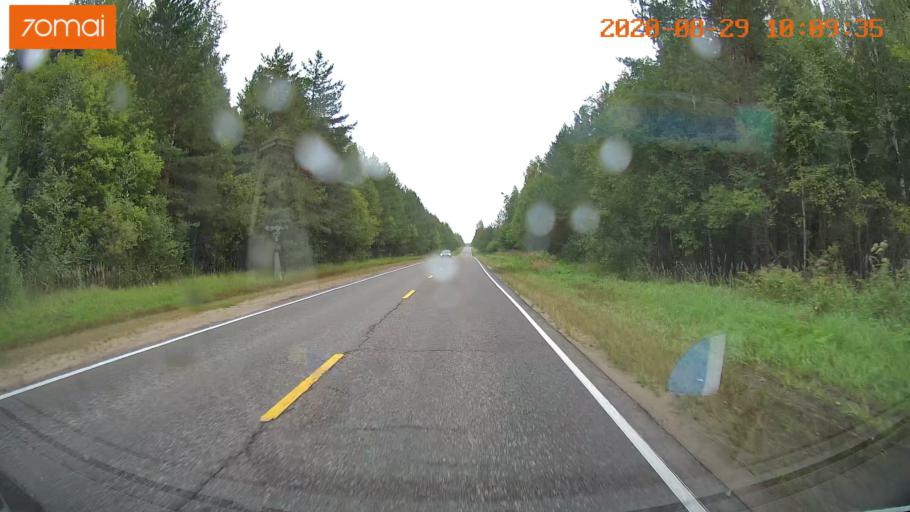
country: RU
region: Ivanovo
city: Kuznechikha
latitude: 57.3753
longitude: 42.6288
